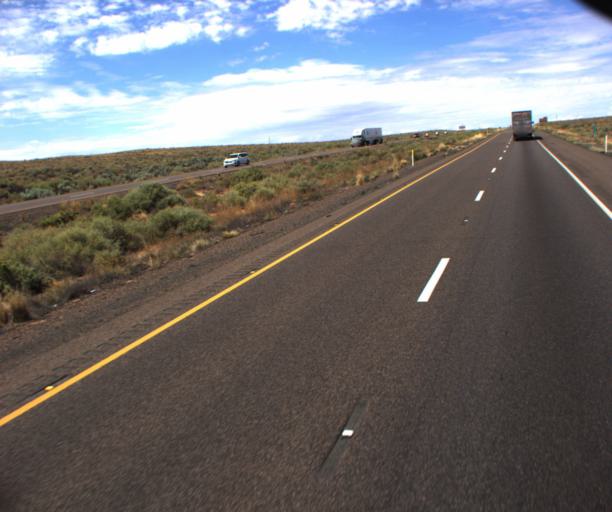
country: US
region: Arizona
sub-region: Navajo County
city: Holbrook
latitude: 35.0696
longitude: -109.7583
